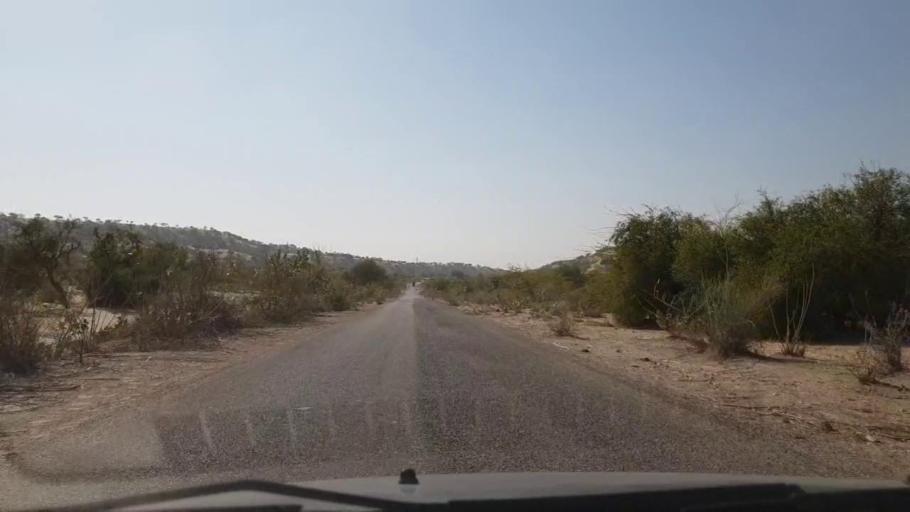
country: PK
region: Sindh
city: Diplo
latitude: 24.5826
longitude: 69.7026
